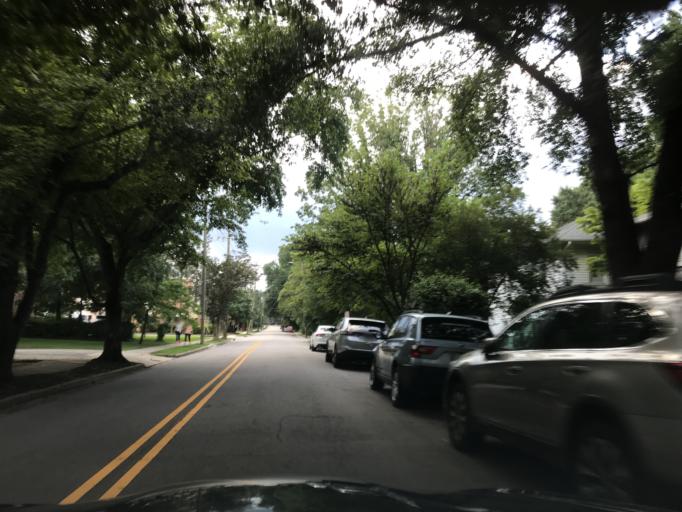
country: US
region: North Carolina
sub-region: Wake County
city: West Raleigh
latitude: 35.8062
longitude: -78.6493
